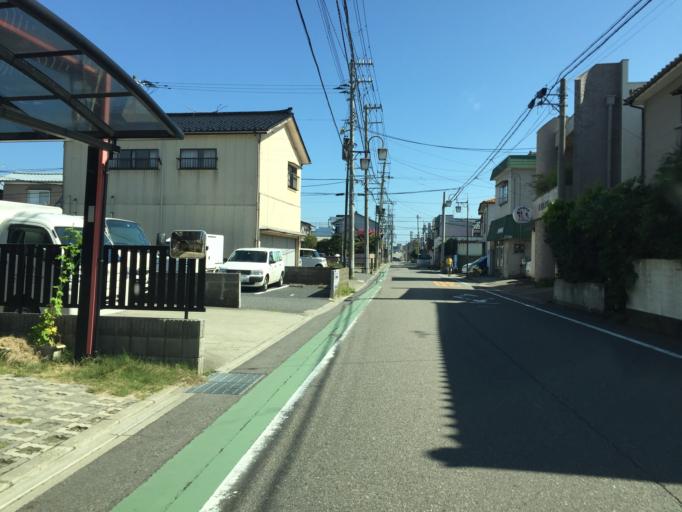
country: JP
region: Niigata
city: Niigata-shi
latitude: 37.9026
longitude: 139.0011
